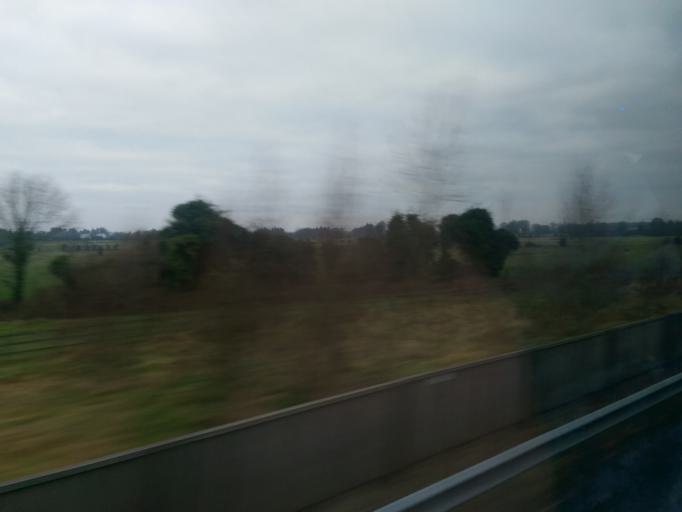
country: IE
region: Connaught
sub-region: County Galway
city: Ballinasloe
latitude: 53.2996
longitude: -8.3437
